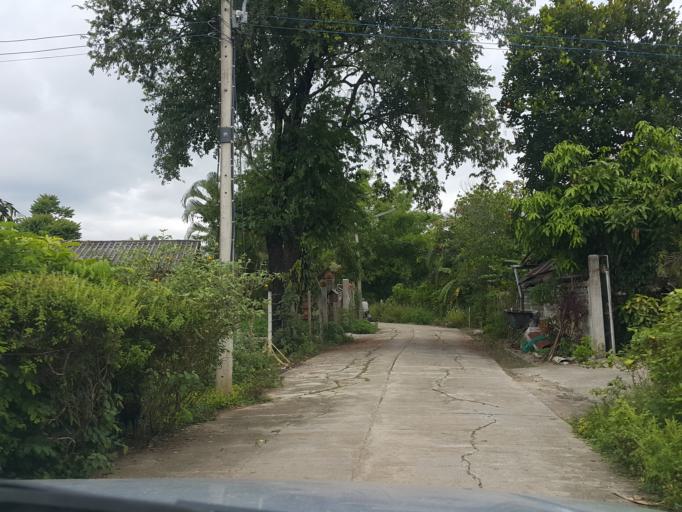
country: TH
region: Chiang Mai
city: San Kamphaeng
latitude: 18.8095
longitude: 99.1407
